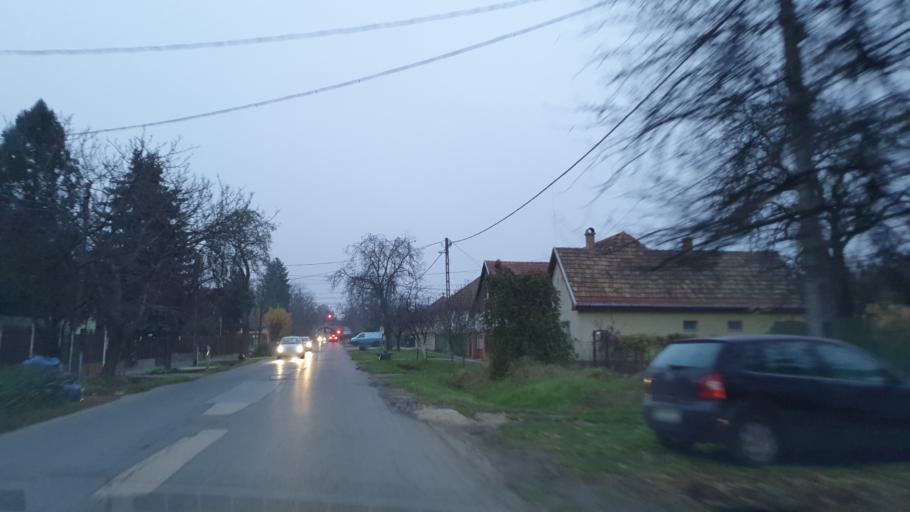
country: HU
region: Pest
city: Csomor
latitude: 47.5276
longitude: 19.2269
